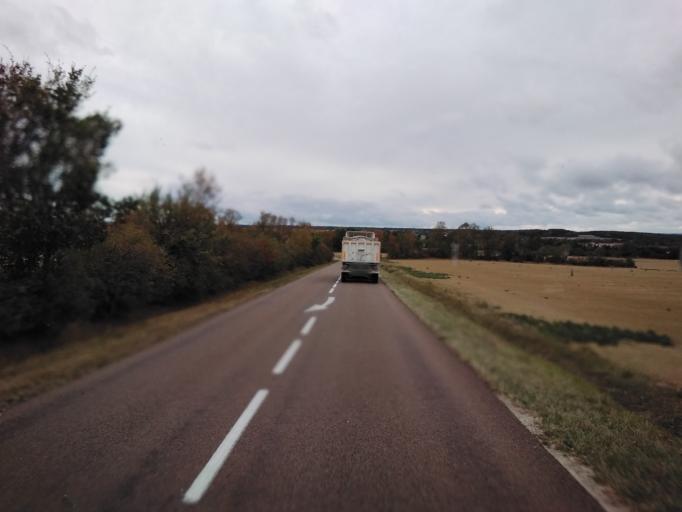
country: FR
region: Champagne-Ardenne
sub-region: Departement de l'Aube
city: Vendeuvre-sur-Barse
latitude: 48.2459
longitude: 4.4813
